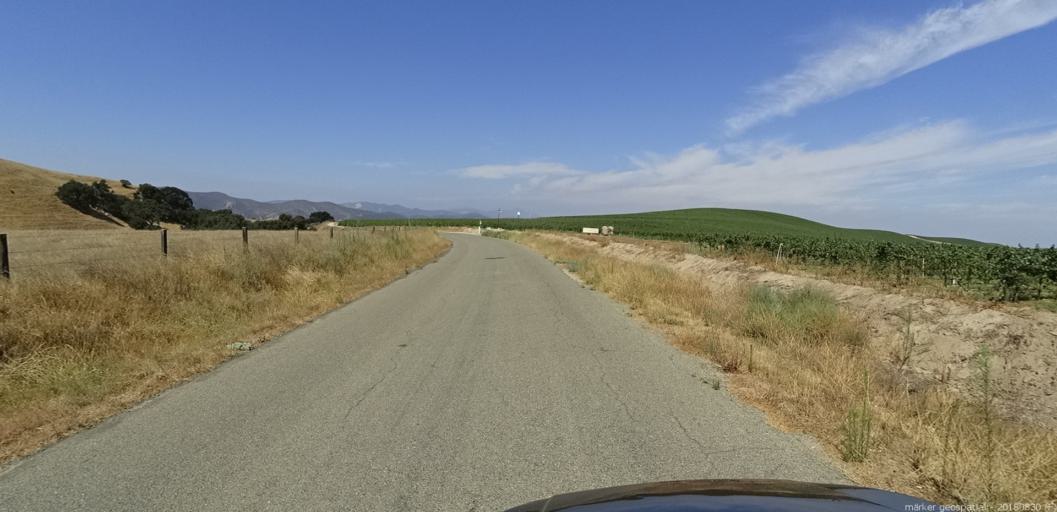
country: US
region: California
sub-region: Monterey County
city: King City
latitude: 36.1129
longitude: -121.0637
